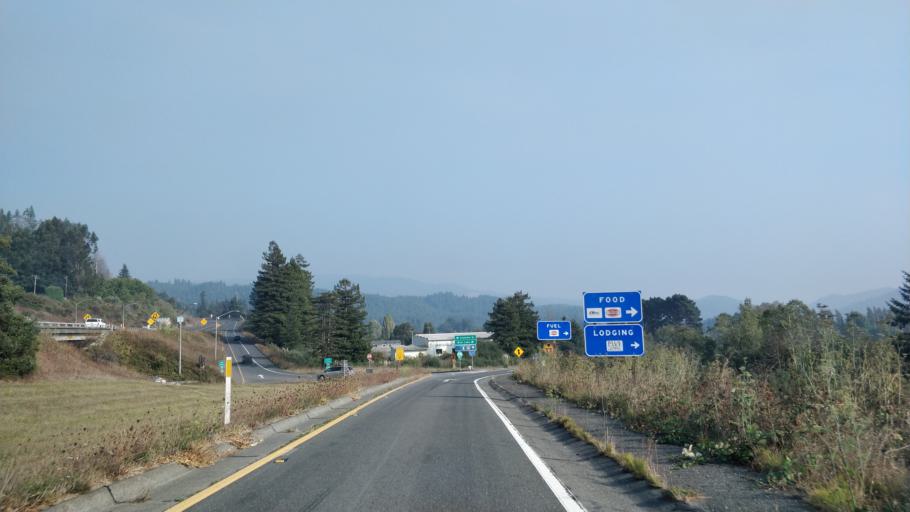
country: US
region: California
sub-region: Humboldt County
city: Blue Lake
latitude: 40.8879
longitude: -123.9987
